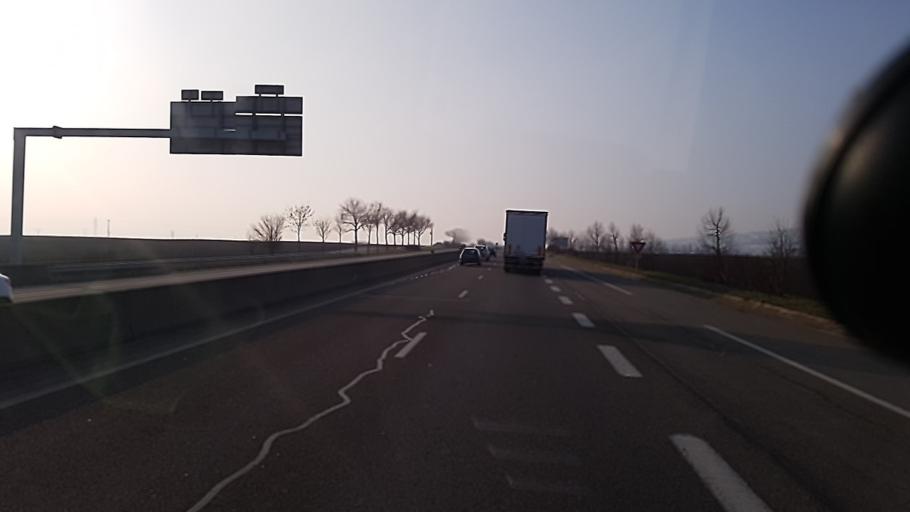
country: FR
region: Alsace
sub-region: Departement du Bas-Rhin
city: Dorlisheim
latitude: 48.5153
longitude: 7.4974
